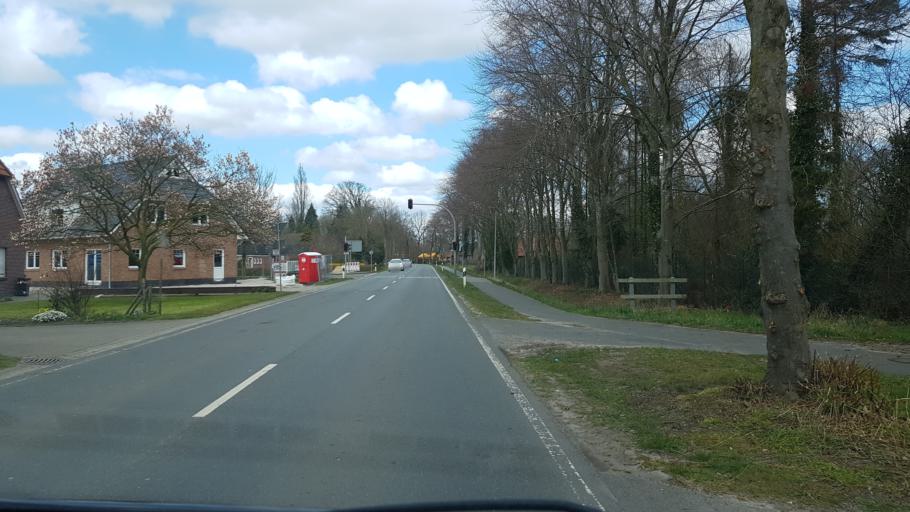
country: DE
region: Lower Saxony
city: Edewecht
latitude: 53.1225
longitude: 7.9300
